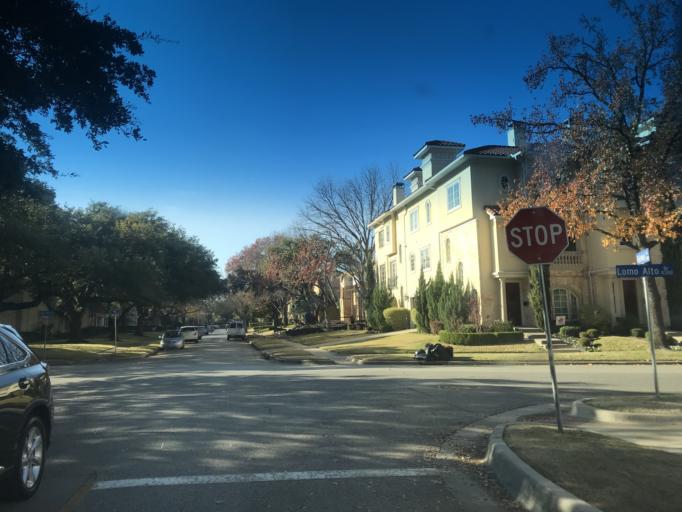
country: US
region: Texas
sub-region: Dallas County
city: Highland Park
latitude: 32.8227
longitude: -96.8127
